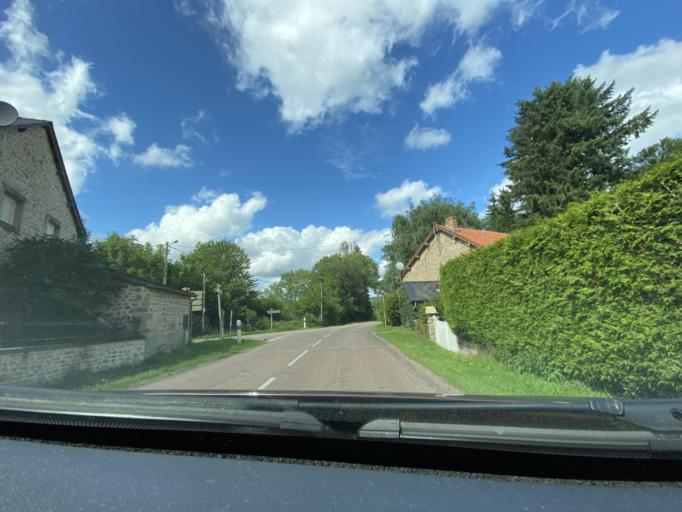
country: FR
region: Bourgogne
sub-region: Departement de la Cote-d'Or
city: Saulieu
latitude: 47.2732
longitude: 4.1278
